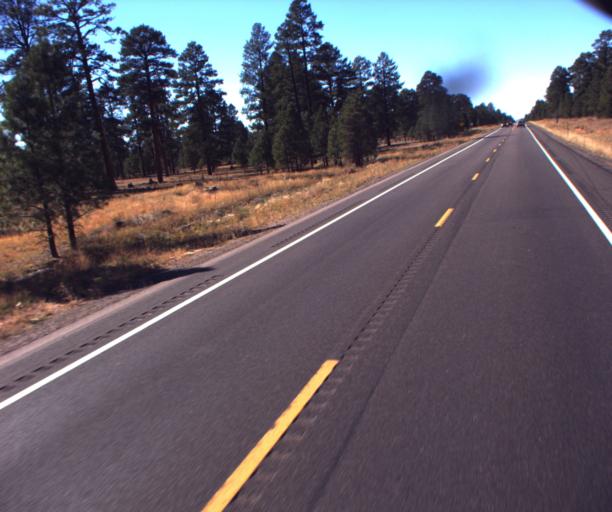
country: US
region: Arizona
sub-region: Apache County
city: Saint Michaels
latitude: 35.6874
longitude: -109.2452
